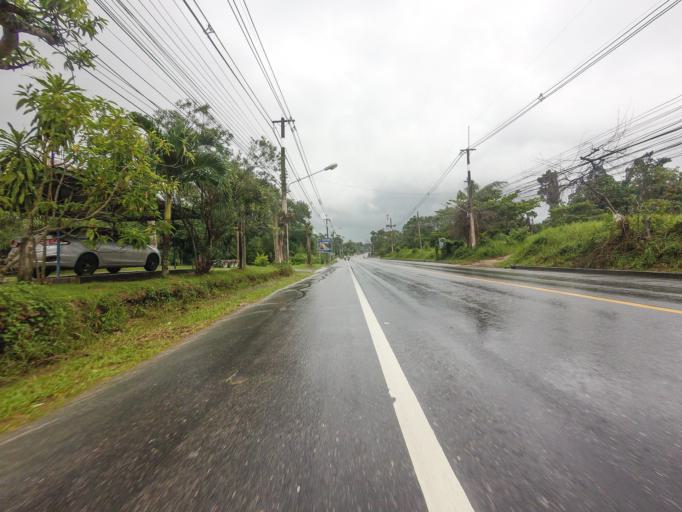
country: TH
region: Surat Thani
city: Ko Samui
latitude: 9.4600
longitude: 99.9837
